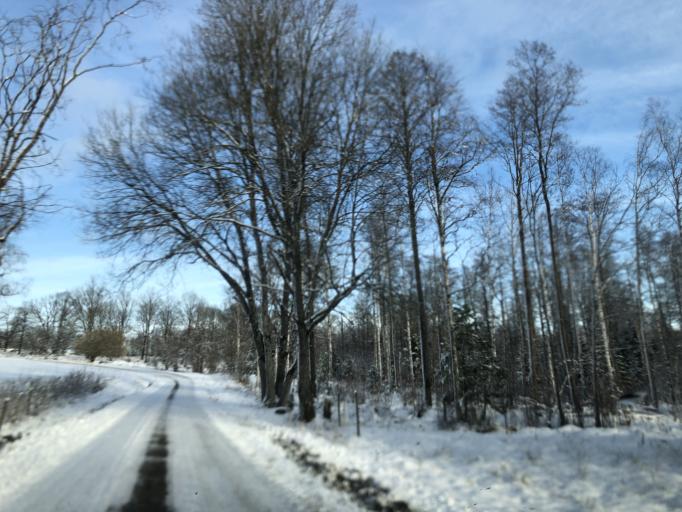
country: SE
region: Vaestra Goetaland
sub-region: Ulricehamns Kommun
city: Ulricehamn
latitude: 57.7317
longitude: 13.4824
